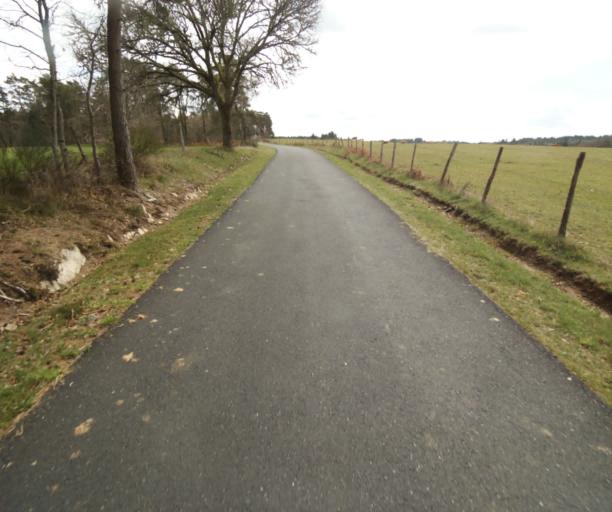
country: FR
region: Limousin
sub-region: Departement de la Correze
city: Correze
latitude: 45.3422
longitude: 1.9540
